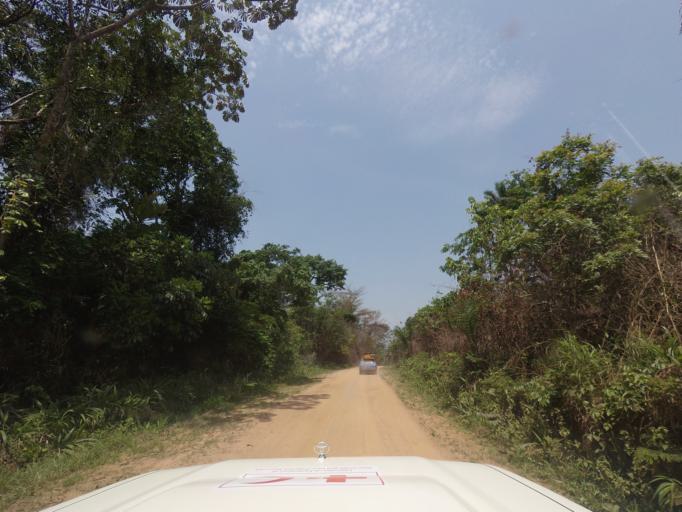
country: LR
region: Lofa
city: Voinjama
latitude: 8.4384
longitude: -9.7099
